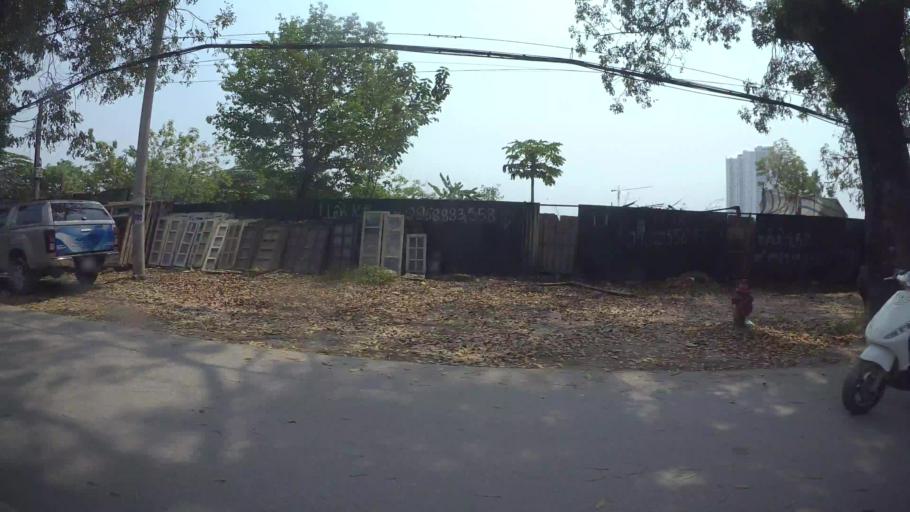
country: VN
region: Ha Noi
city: Ha Dong
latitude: 20.9924
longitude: 105.7620
